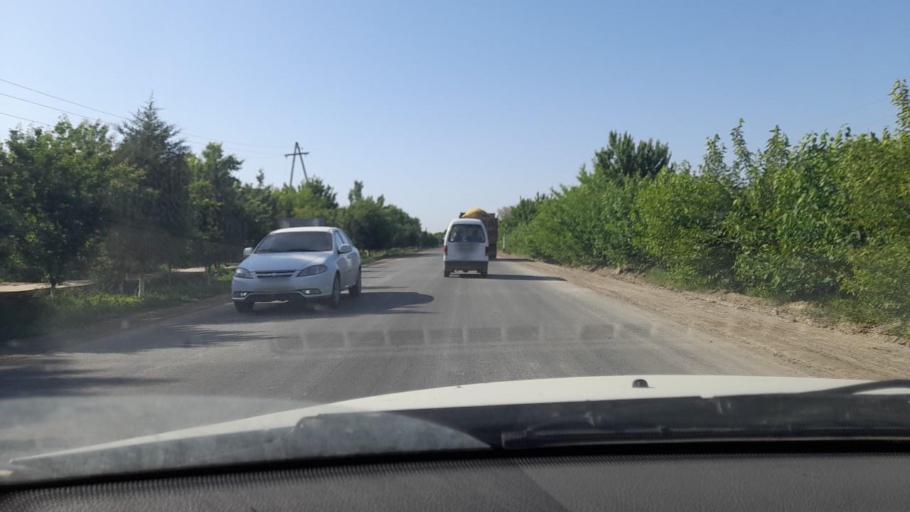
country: UZ
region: Bukhara
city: Romiton
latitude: 40.0550
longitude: 64.3280
